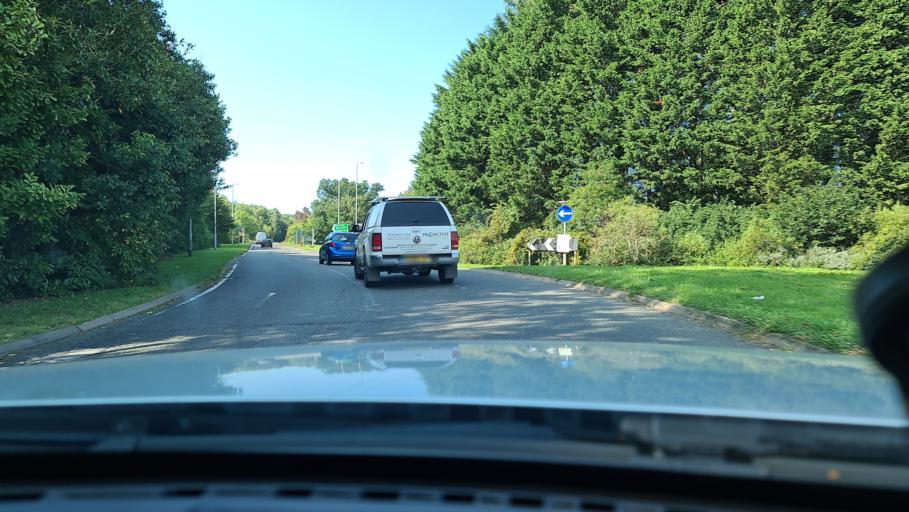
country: GB
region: England
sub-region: Northamptonshire
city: Daventry
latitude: 52.2468
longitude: -1.1505
